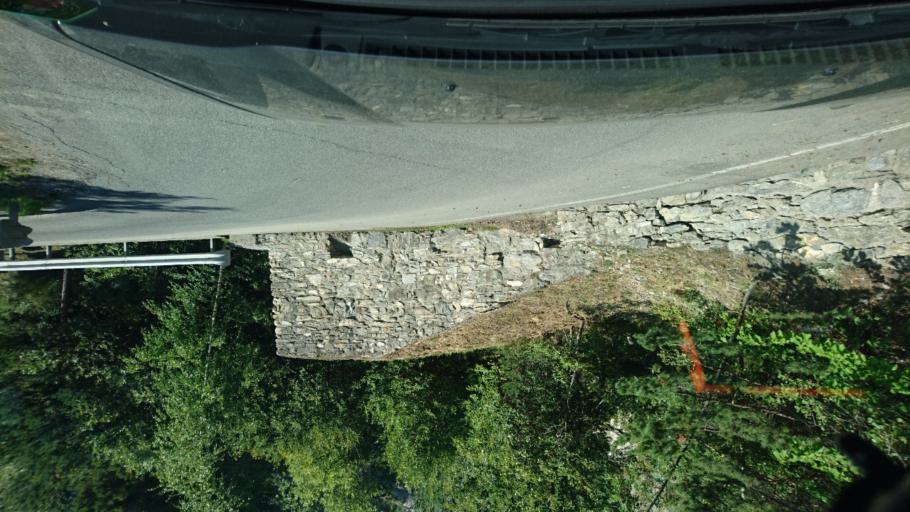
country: IT
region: Aosta Valley
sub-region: Valle d'Aosta
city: Villeneuve
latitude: 45.7260
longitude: 7.1976
